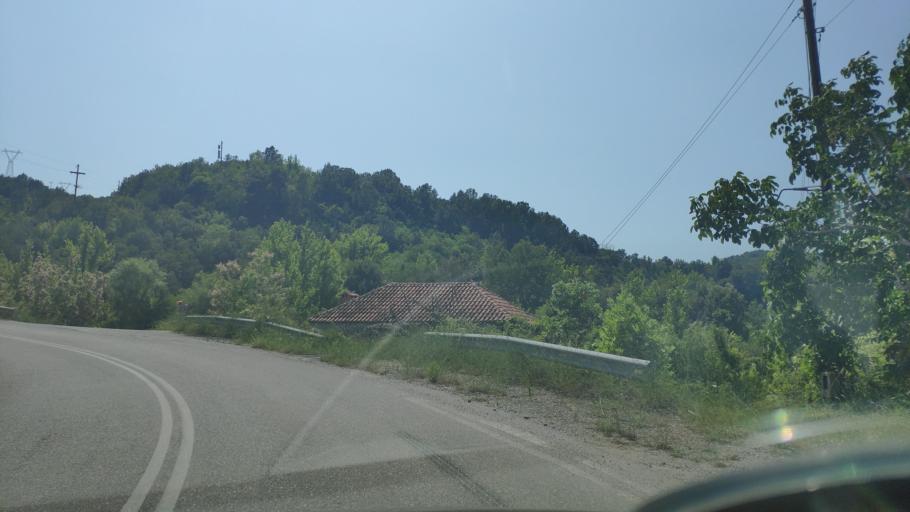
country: GR
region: Epirus
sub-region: Nomos Artas
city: Ano Kalentini
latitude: 39.2275
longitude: 21.1483
